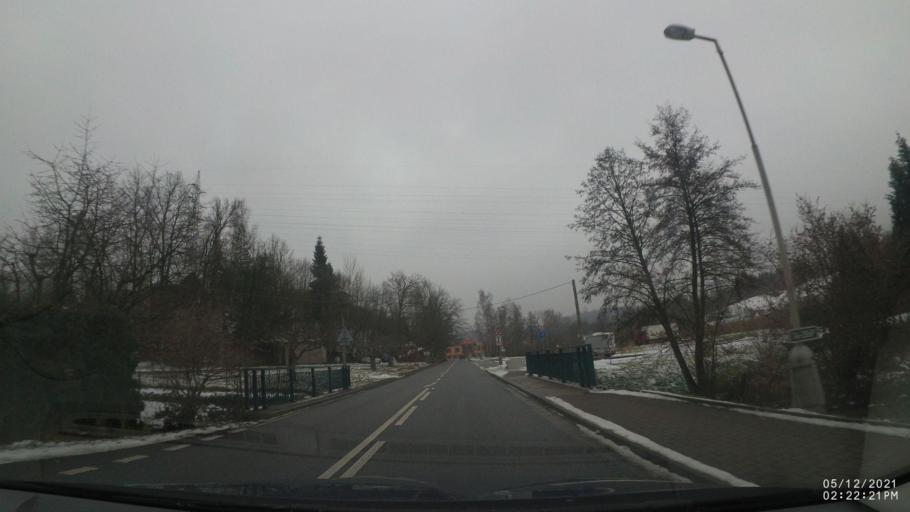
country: CZ
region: Kralovehradecky
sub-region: Okres Nachod
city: Nachod
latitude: 50.4328
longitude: 16.1585
